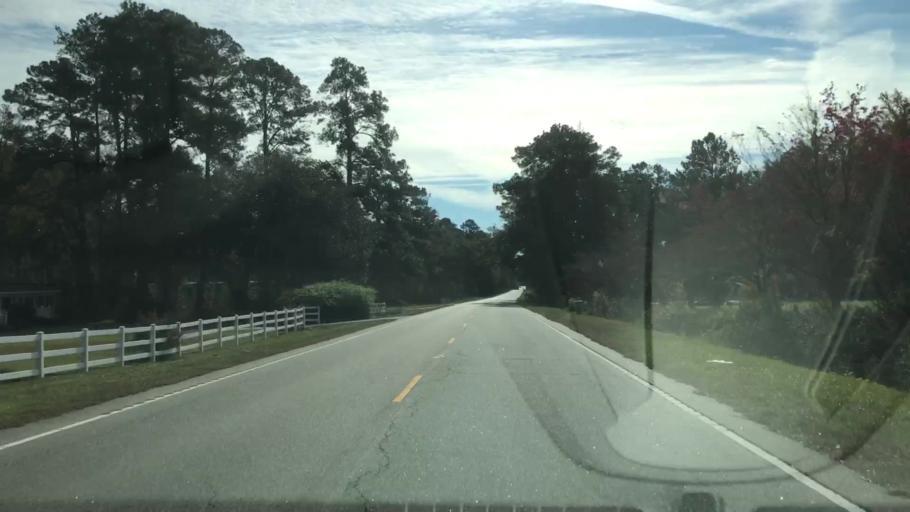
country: US
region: South Carolina
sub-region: Colleton County
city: Walterboro
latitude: 32.8490
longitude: -80.5937
